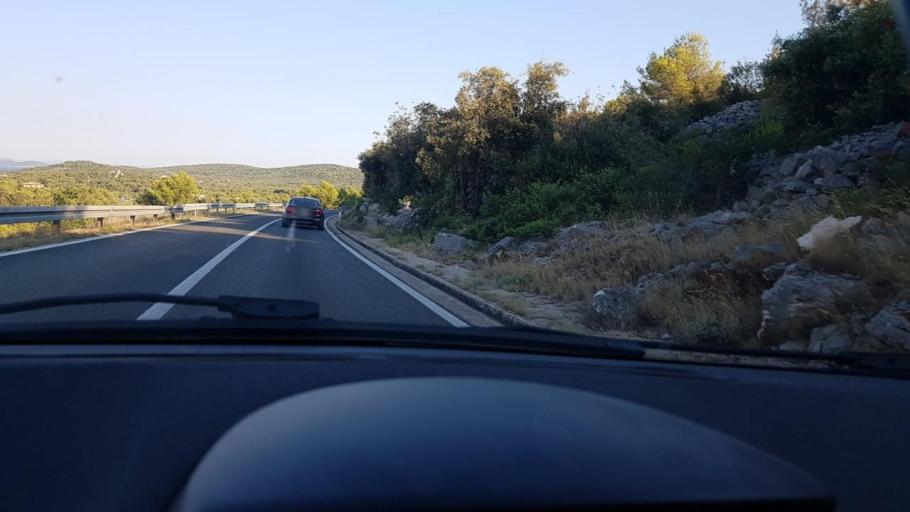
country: HR
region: Sibensko-Kniniska
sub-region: Grad Sibenik
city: Tisno
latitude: 43.7941
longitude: 15.6241
